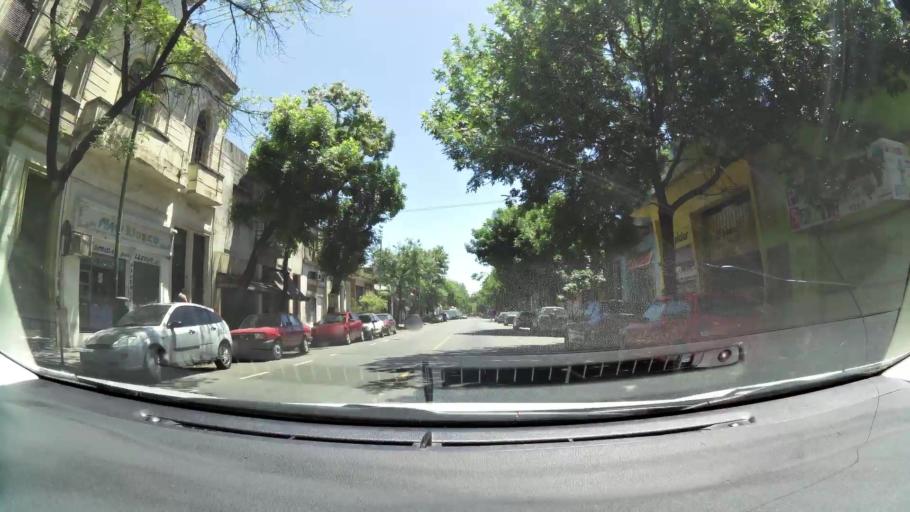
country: AR
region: Buenos Aires
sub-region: Partido de Avellaneda
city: Avellaneda
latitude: -34.6473
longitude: -58.3778
